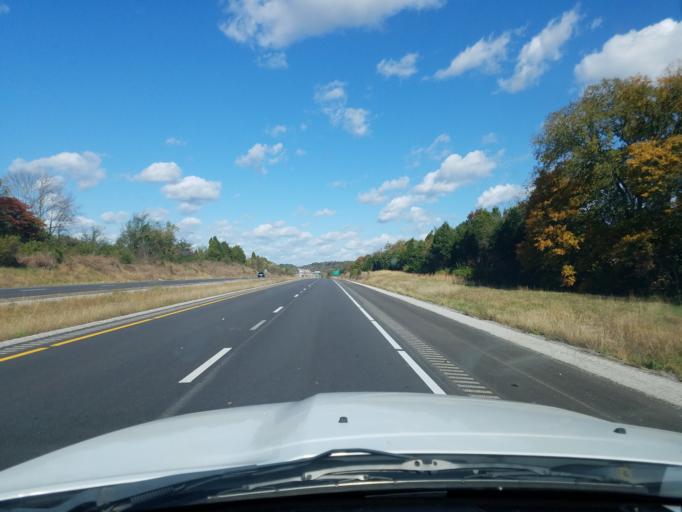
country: US
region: Kentucky
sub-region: Warren County
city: Bowling Green
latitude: 36.9817
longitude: -86.5016
